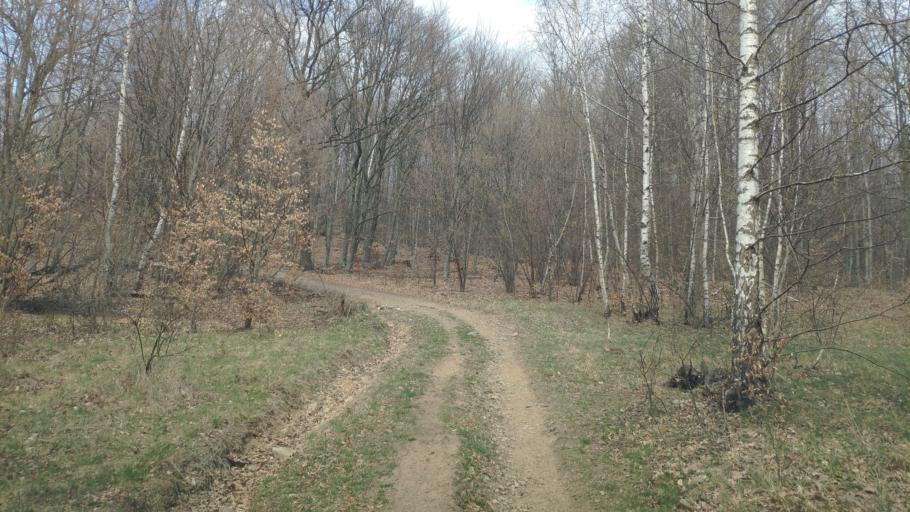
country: SK
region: Kosicky
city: Gelnica
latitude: 48.7510
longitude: 21.0190
